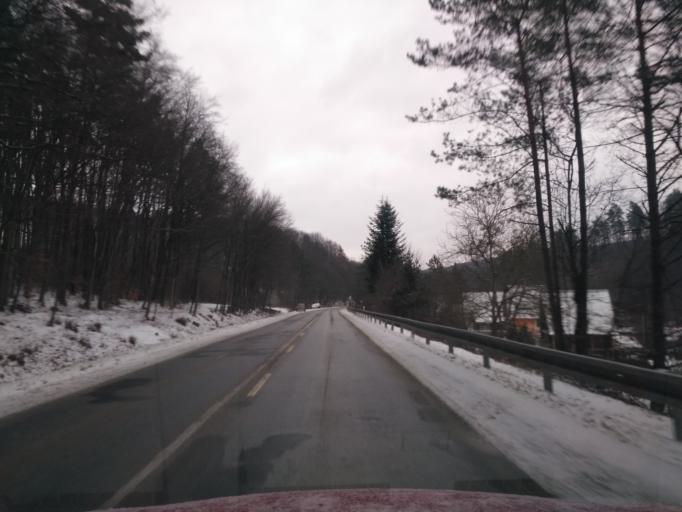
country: SK
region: Presovsky
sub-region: Okres Presov
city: Presov
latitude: 48.9750
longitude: 21.1709
